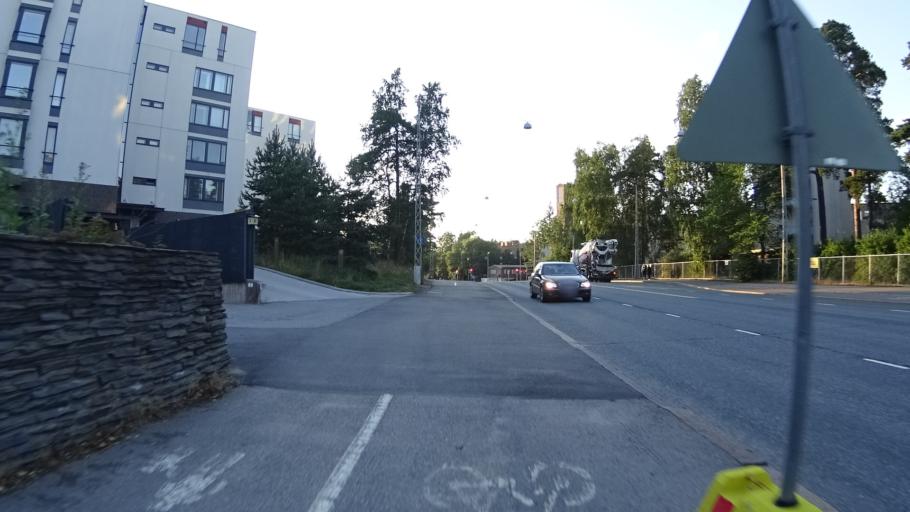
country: FI
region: Uusimaa
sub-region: Helsinki
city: Helsinki
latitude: 60.1901
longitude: 24.9016
